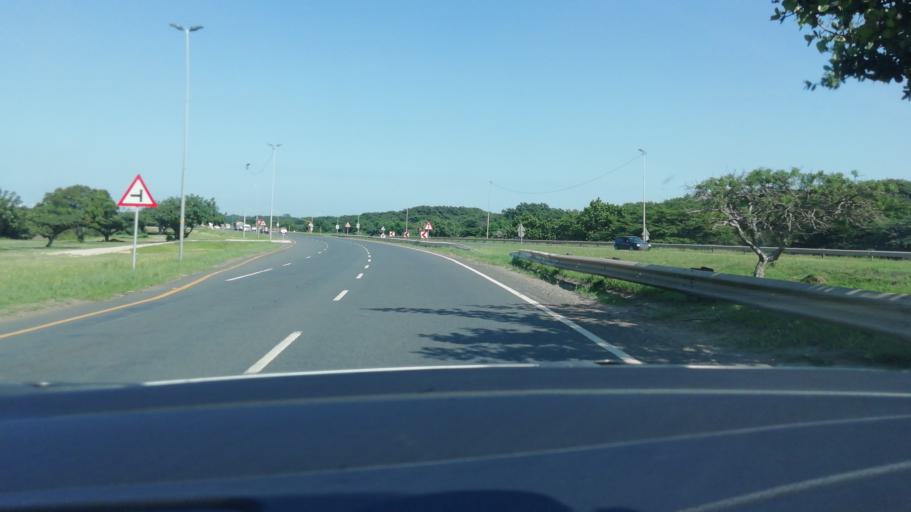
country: ZA
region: KwaZulu-Natal
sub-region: uThungulu District Municipality
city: Richards Bay
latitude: -28.7736
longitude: 32.0713
